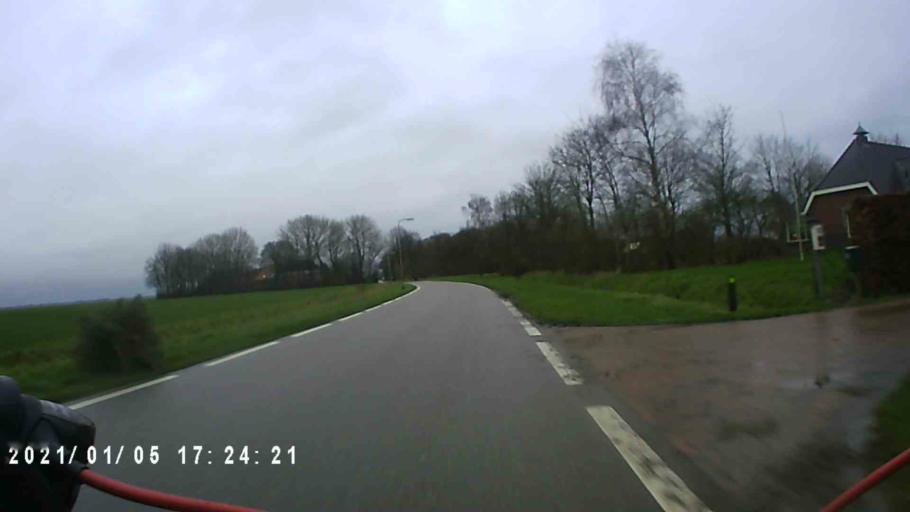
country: NL
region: Groningen
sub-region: Gemeente Delfzijl
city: Delfzijl
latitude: 53.2326
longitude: 6.9641
